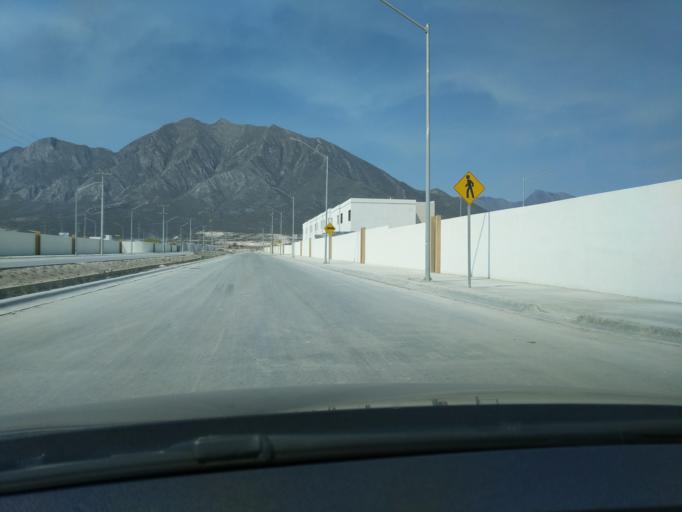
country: MX
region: Nuevo Leon
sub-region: Garcia
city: Valle de Lincoln
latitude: 25.7946
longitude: -100.4710
